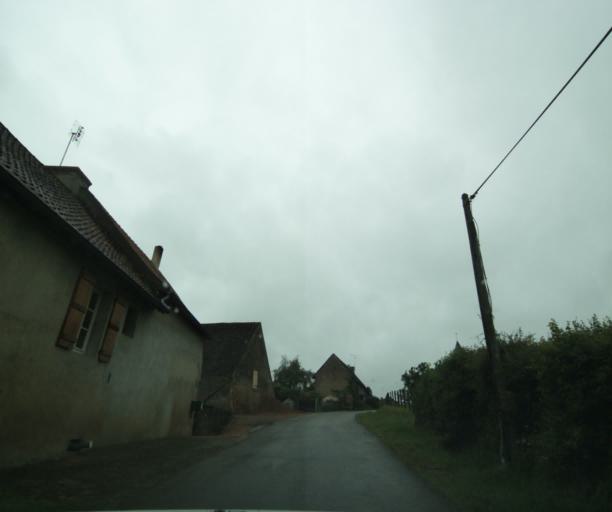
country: FR
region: Bourgogne
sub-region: Departement de Saone-et-Loire
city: Charolles
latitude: 46.4125
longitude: 4.3116
